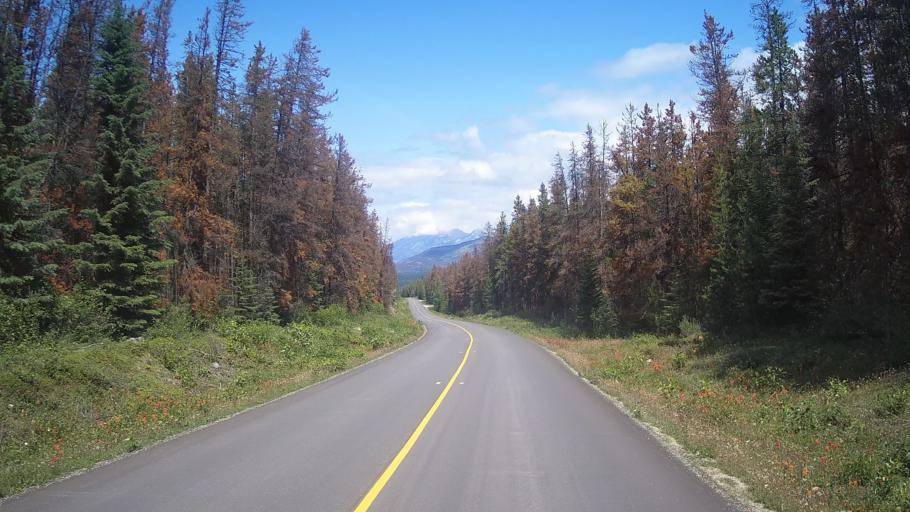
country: CA
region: Alberta
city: Jasper Park Lodge
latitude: 52.7766
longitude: -118.0326
